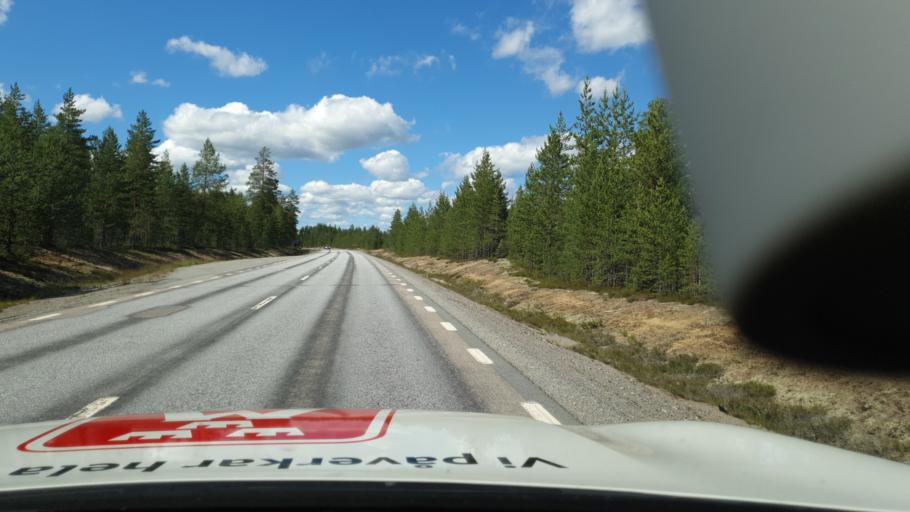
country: SE
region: Vaesterbotten
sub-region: Umea Kommun
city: Roback
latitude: 63.9644
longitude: 20.1266
